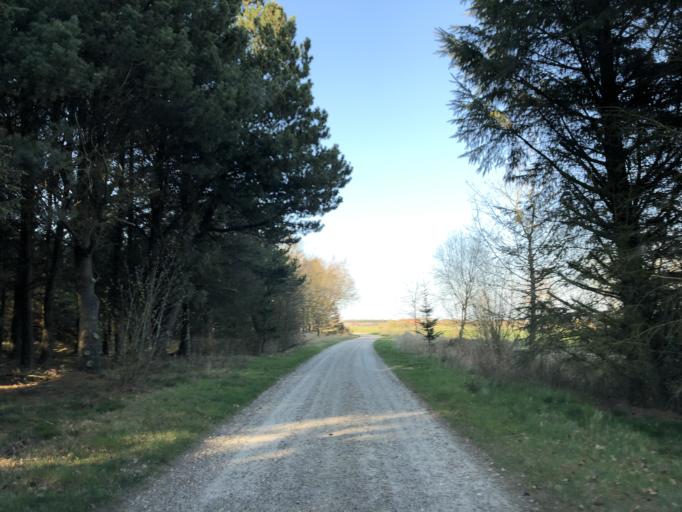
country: DK
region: Central Jutland
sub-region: Holstebro Kommune
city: Ulfborg
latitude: 56.3519
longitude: 8.2466
